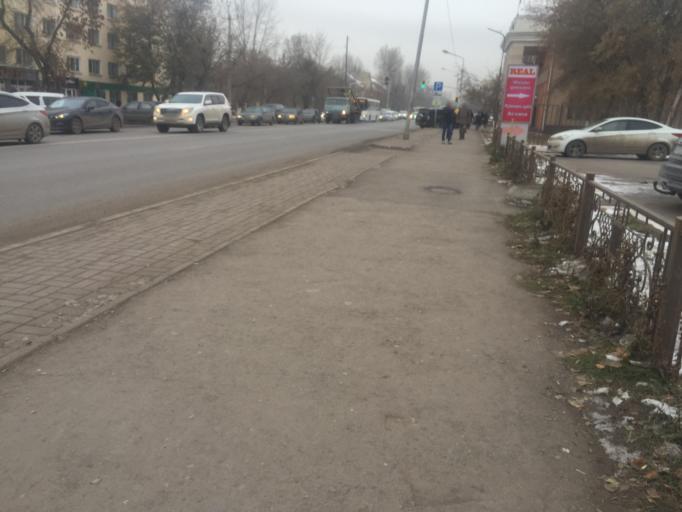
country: KZ
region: Astana Qalasy
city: Astana
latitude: 51.1821
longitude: 71.4228
